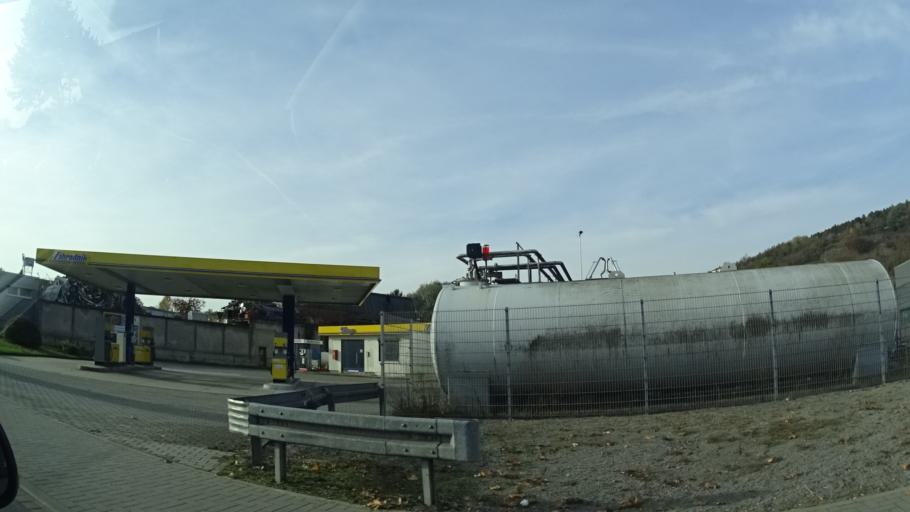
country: DE
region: Baden-Wuerttemberg
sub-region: Karlsruhe Region
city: Neckarzimmern
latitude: 49.3428
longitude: 9.1228
